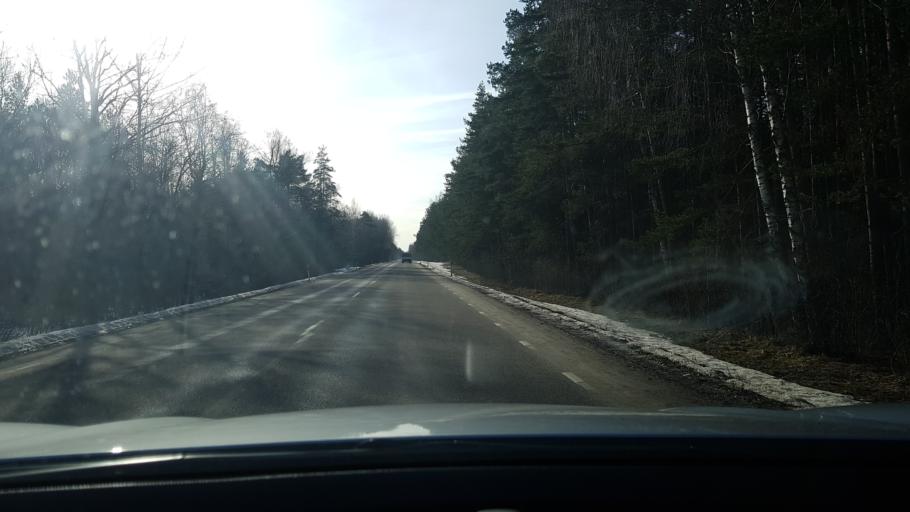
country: EE
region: Saare
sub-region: Orissaare vald
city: Orissaare
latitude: 58.5540
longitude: 23.0644
